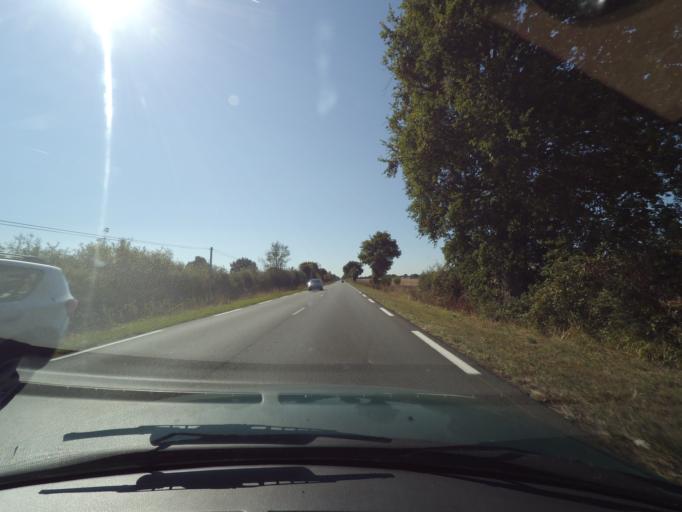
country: FR
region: Poitou-Charentes
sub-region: Departement de la Vienne
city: Saulge
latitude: 46.3138
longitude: 0.8268
